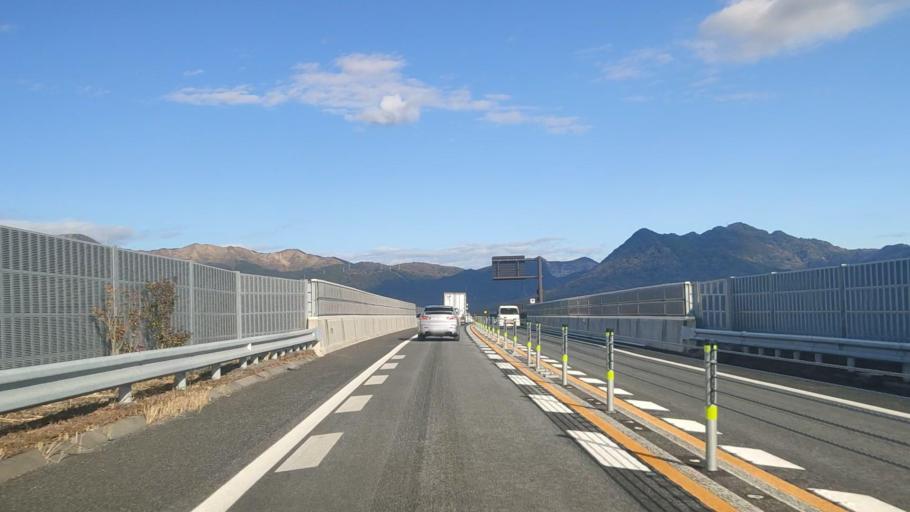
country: JP
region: Fukuoka
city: Yukuhashi
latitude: 33.7285
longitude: 130.9475
